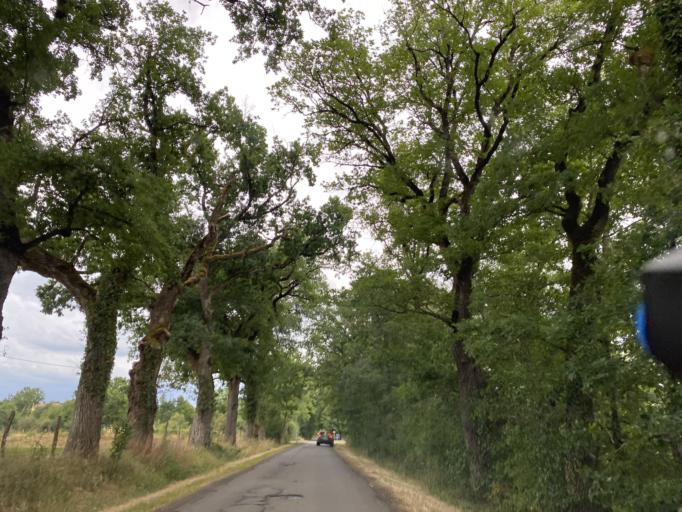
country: FR
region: Auvergne
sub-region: Departement du Puy-de-Dome
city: Courpiere
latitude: 45.7464
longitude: 3.4563
